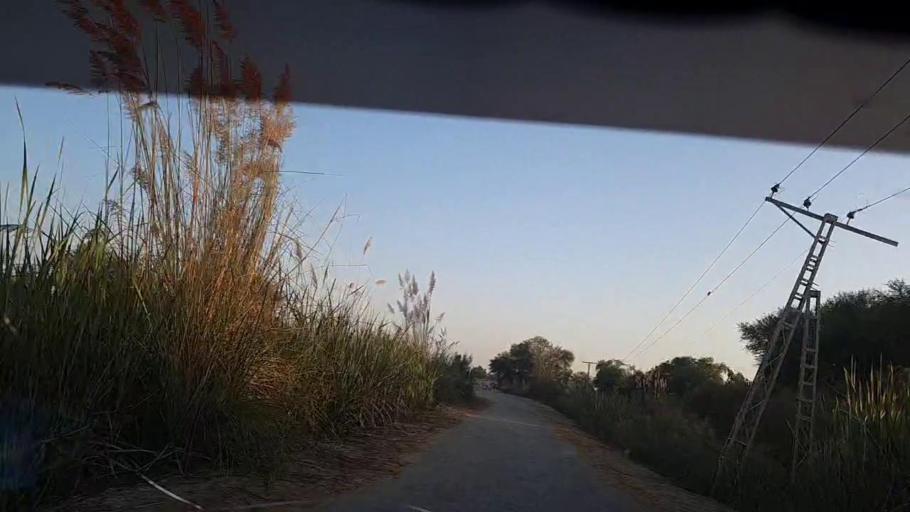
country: PK
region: Sindh
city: Ratodero
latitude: 27.9044
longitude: 68.2399
